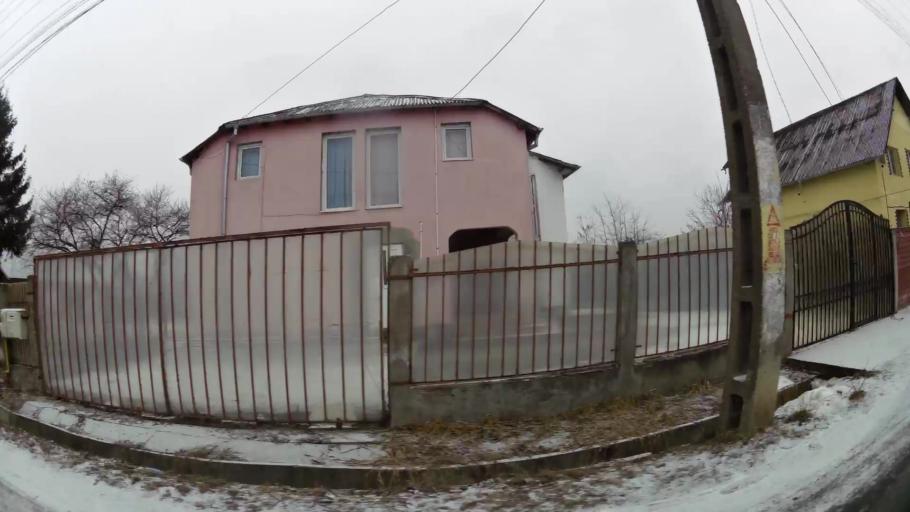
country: RO
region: Dambovita
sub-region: Comuna Aninoasa
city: Viforata
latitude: 44.9429
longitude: 25.4725
